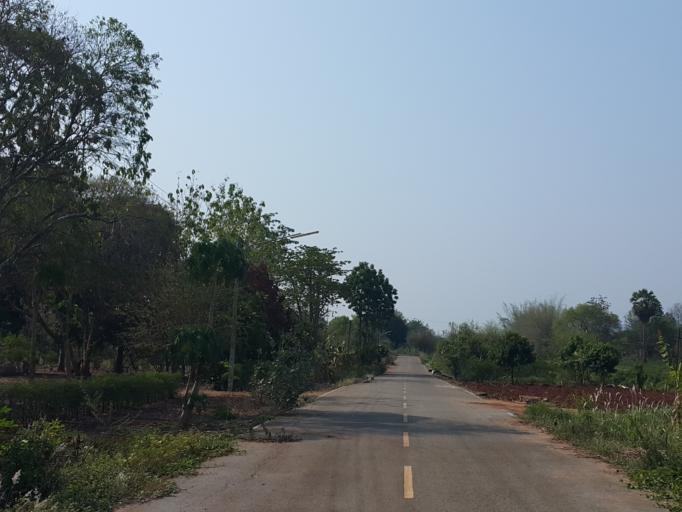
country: TH
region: Kanchanaburi
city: Sai Yok
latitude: 14.1304
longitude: 99.1295
